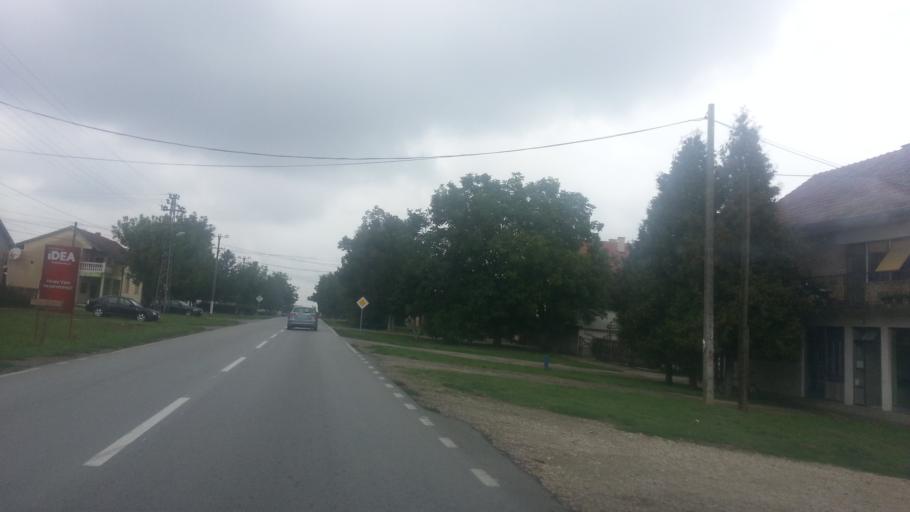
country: RS
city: Stari Banovci
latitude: 44.9772
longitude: 20.2810
